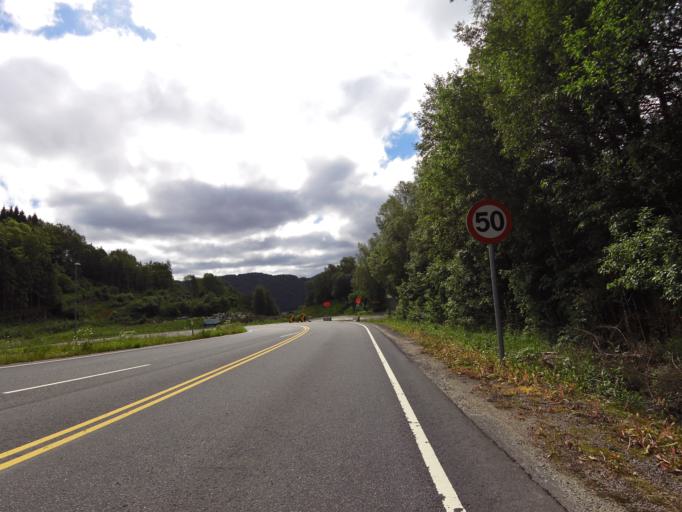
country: NO
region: Vest-Agder
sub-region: Flekkefjord
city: Flekkefjord
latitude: 58.2656
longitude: 6.8076
